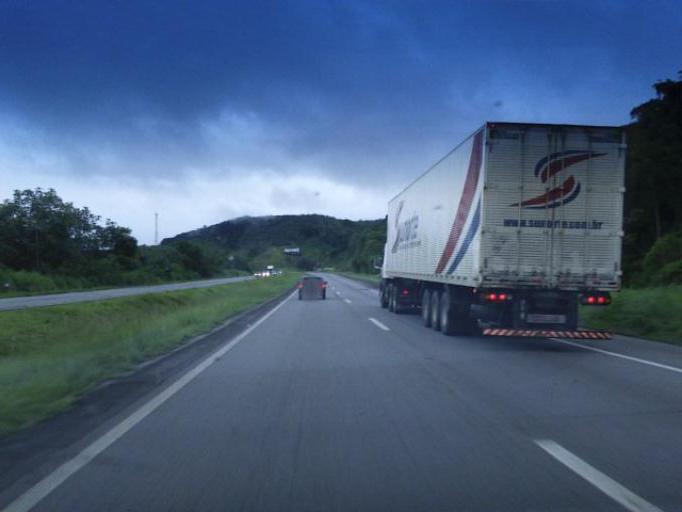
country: BR
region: Sao Paulo
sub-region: Miracatu
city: Miracatu
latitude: -24.2238
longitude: -47.3647
